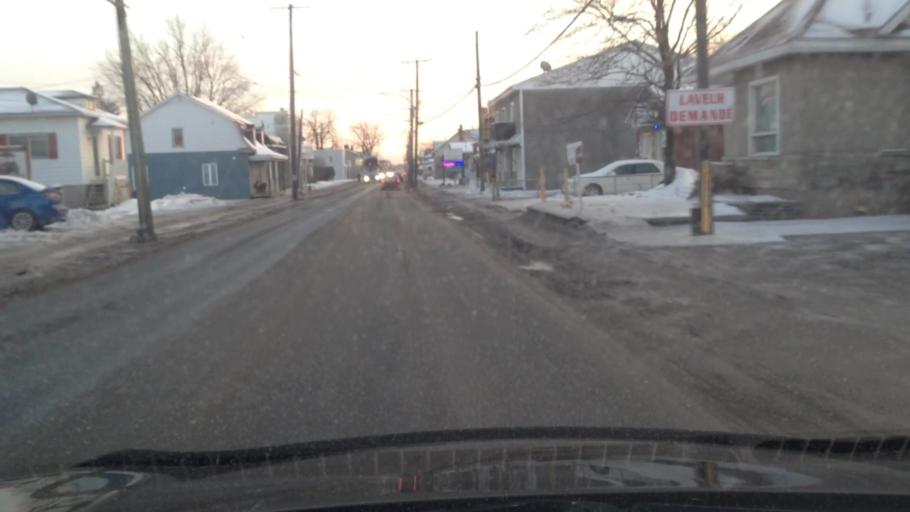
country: CA
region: Quebec
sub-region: Lanaudiere
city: Saint-Lin-Laurentides
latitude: 45.8588
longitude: -73.7571
